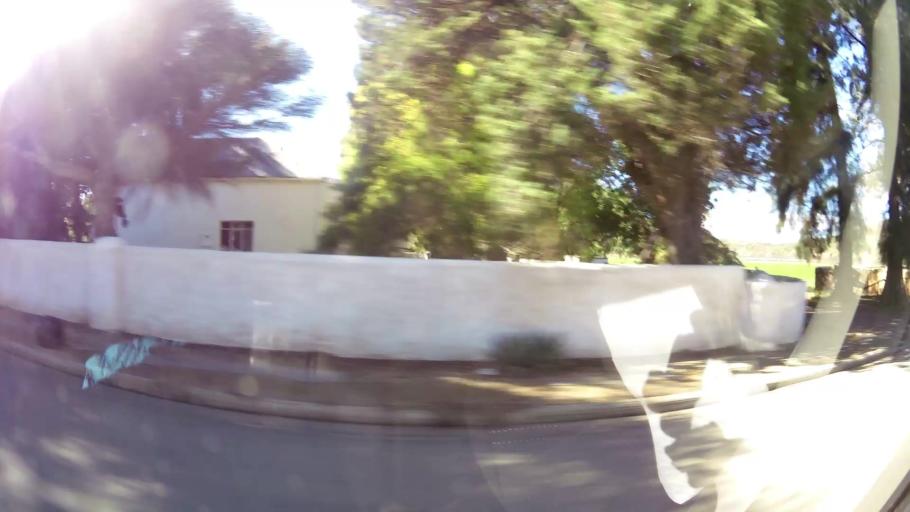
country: ZA
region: Western Cape
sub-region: Cape Winelands District Municipality
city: Ashton
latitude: -33.7861
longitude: 20.1278
